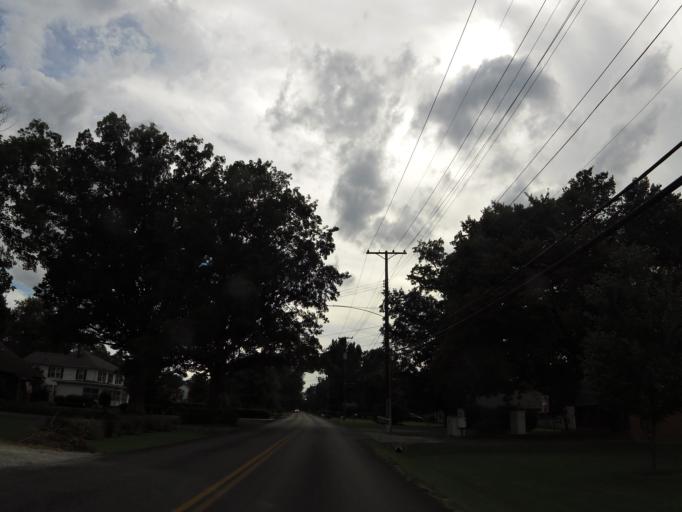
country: US
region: Kentucky
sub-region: Christian County
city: Hopkinsville
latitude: 36.8543
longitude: -87.5023
